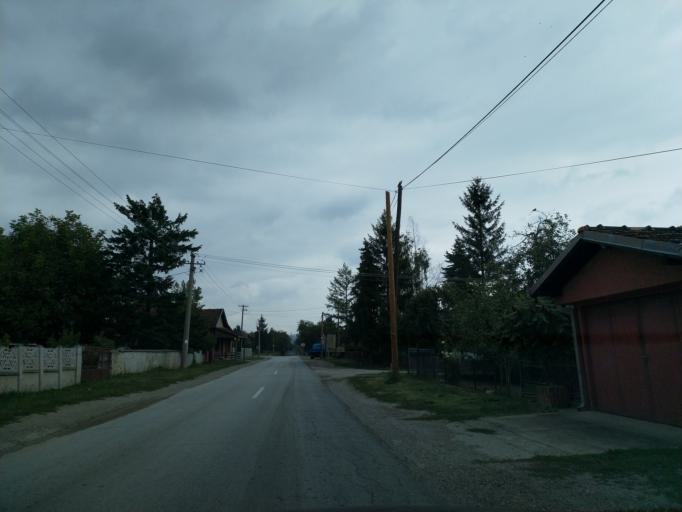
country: RS
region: Central Serbia
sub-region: Sumadijski Okrug
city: Batocina
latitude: 44.0793
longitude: 21.1815
